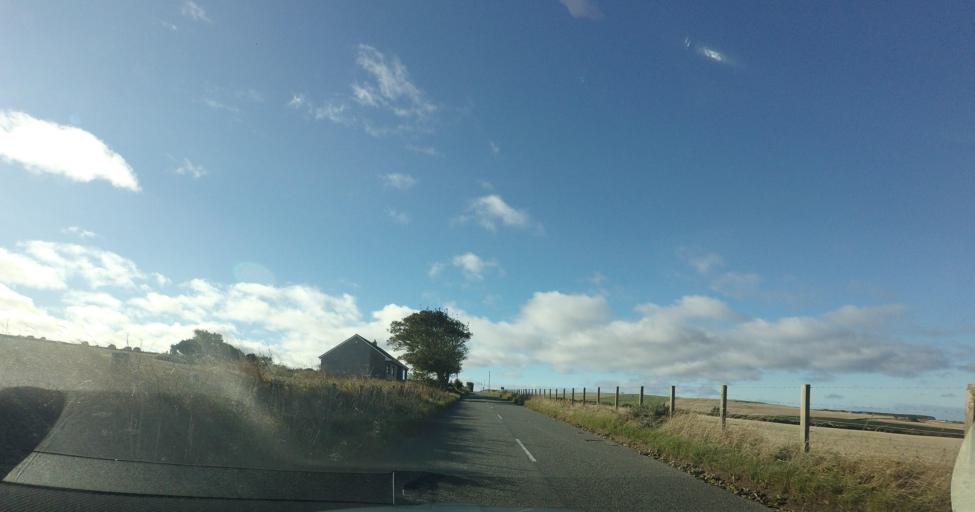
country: GB
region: Scotland
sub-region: Aberdeenshire
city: Macduff
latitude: 57.6681
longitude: -2.3070
